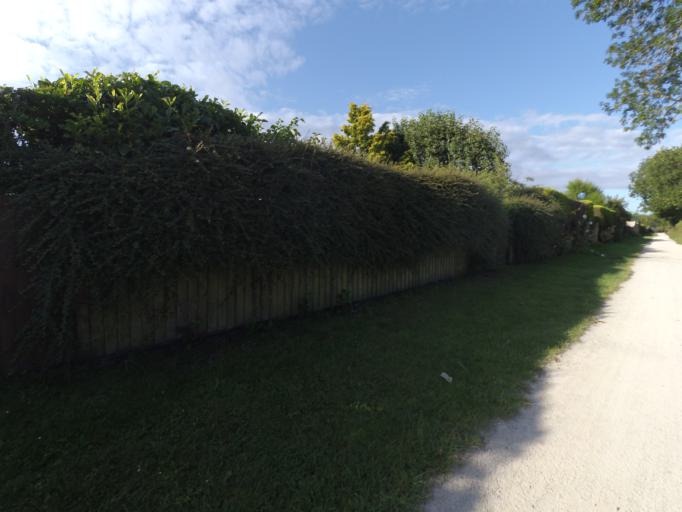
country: GB
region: England
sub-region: Staffordshire
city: Stafford
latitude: 52.8033
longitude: -2.1640
